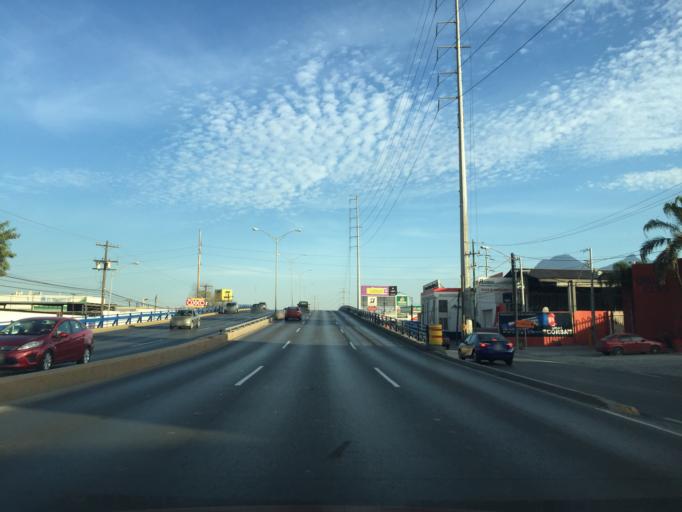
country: MX
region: Nuevo Leon
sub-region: San Nicolas de los Garza
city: San Nicolas de los Garza
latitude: 25.7166
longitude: -100.2852
